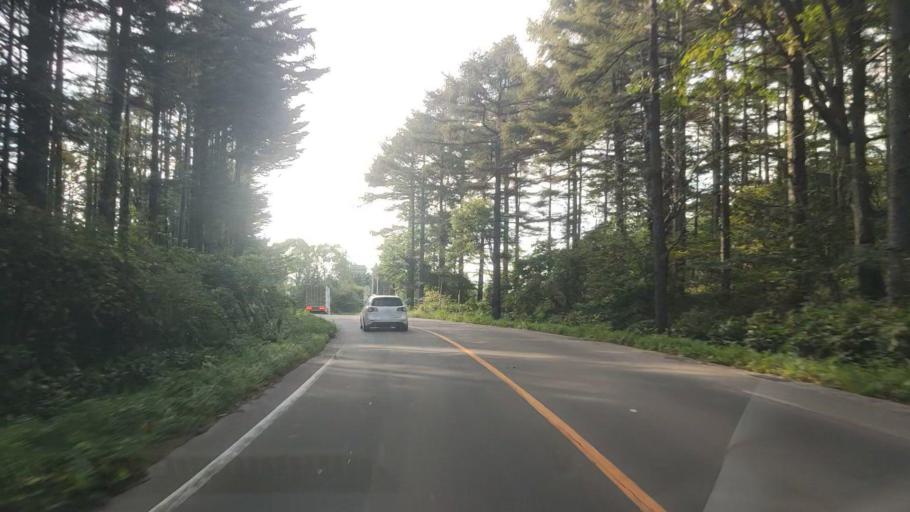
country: JP
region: Nagano
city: Ueda
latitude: 36.4902
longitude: 138.3978
